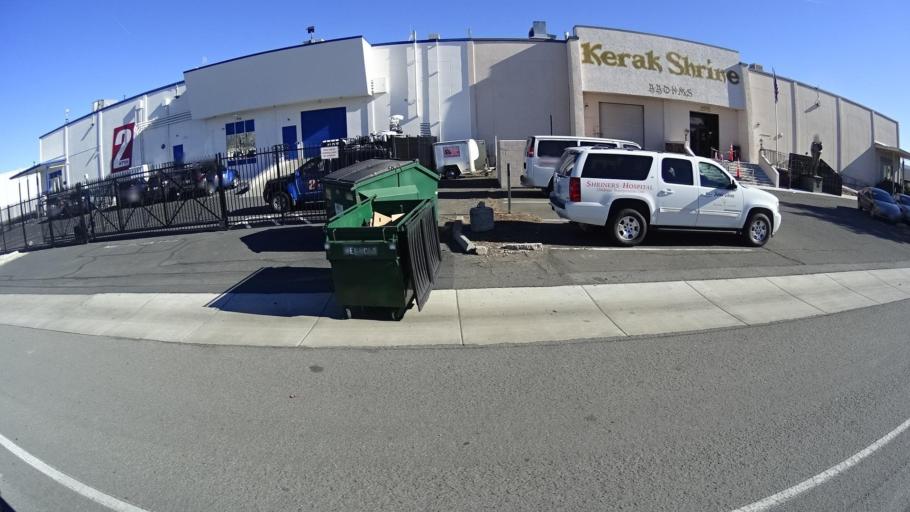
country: US
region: Nevada
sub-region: Washoe County
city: Sparks
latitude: 39.5065
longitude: -119.7618
